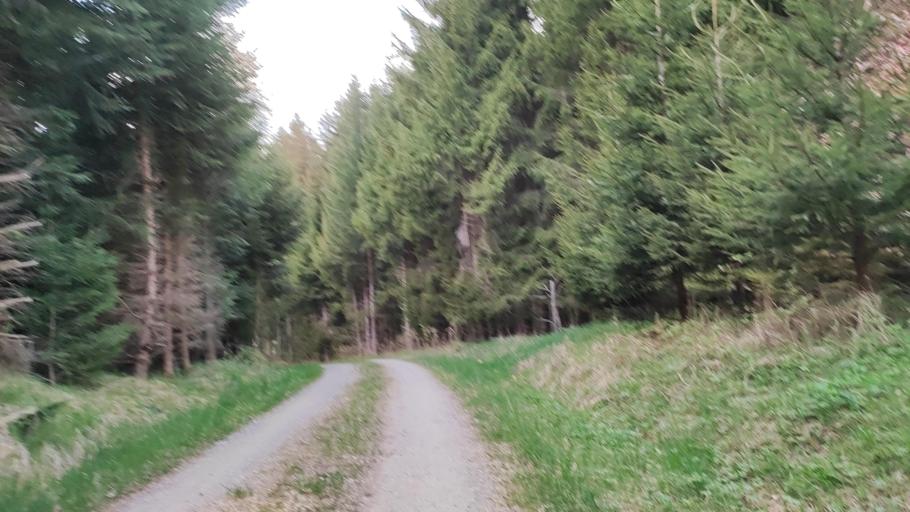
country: DE
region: Bavaria
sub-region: Swabia
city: Zusmarshausen
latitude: 48.3916
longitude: 10.5548
